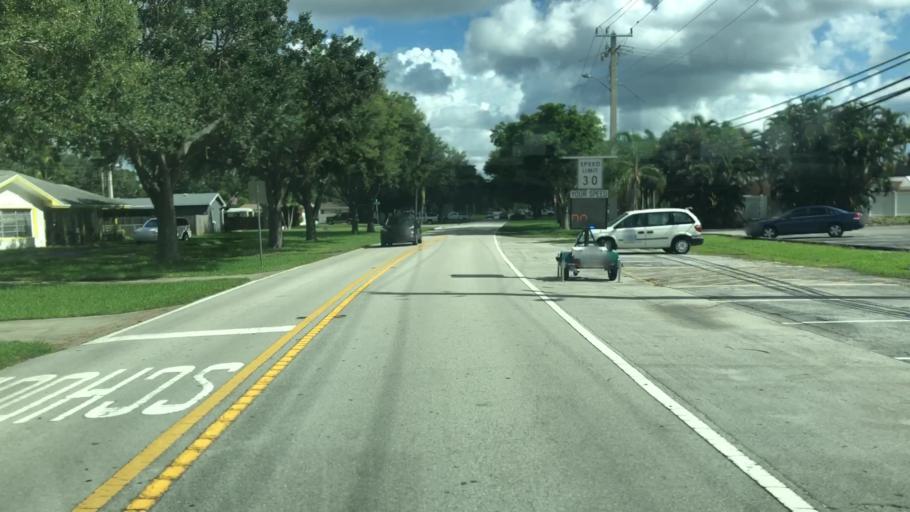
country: US
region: Florida
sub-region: Broward County
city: Cooper City
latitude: 26.0595
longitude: -80.2708
